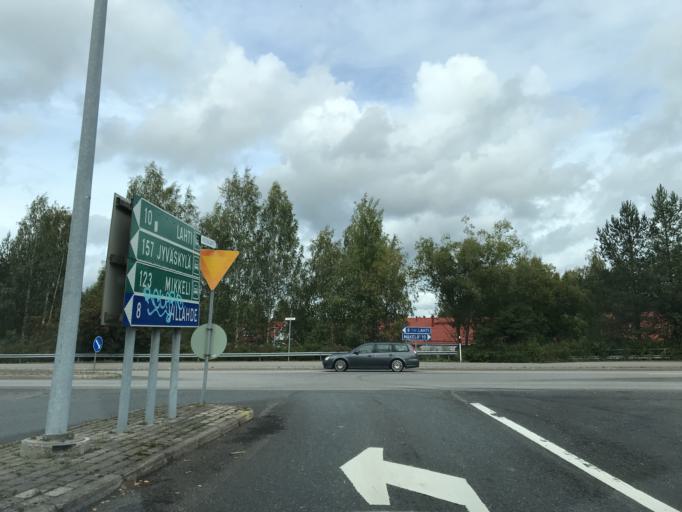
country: FI
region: Paijanne Tavastia
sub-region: Lahti
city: Lahti
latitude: 61.0024
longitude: 25.7758
